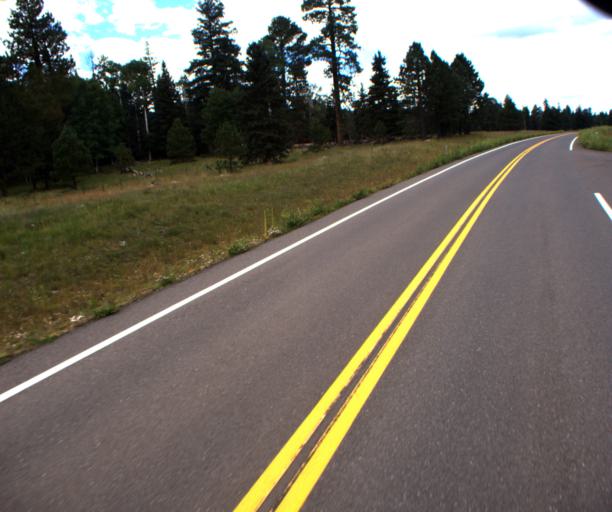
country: US
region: Arizona
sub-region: Apache County
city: Eagar
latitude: 33.9852
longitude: -109.5080
